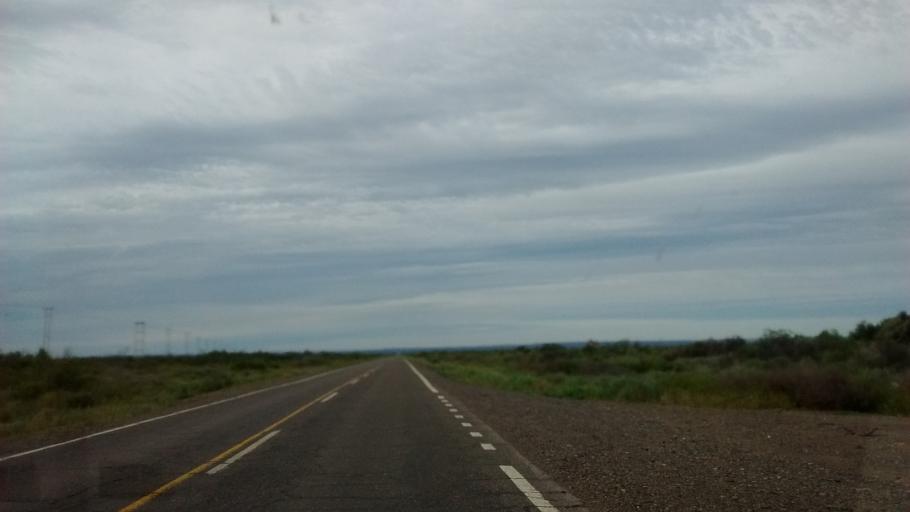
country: AR
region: Rio Negro
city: Catriel
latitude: -37.9850
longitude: -67.9089
